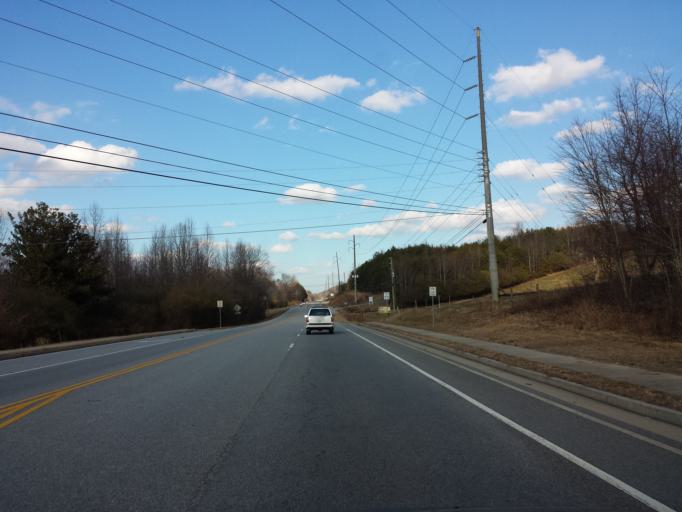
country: US
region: Georgia
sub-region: White County
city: Cleveland
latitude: 34.6310
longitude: -83.7500
